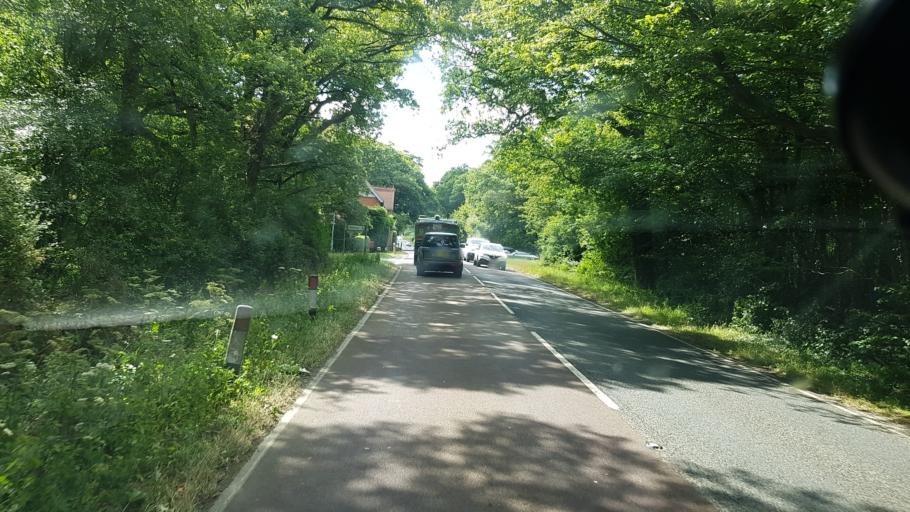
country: GB
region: England
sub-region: West Sussex
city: Southwater
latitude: 50.9936
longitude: -0.3609
